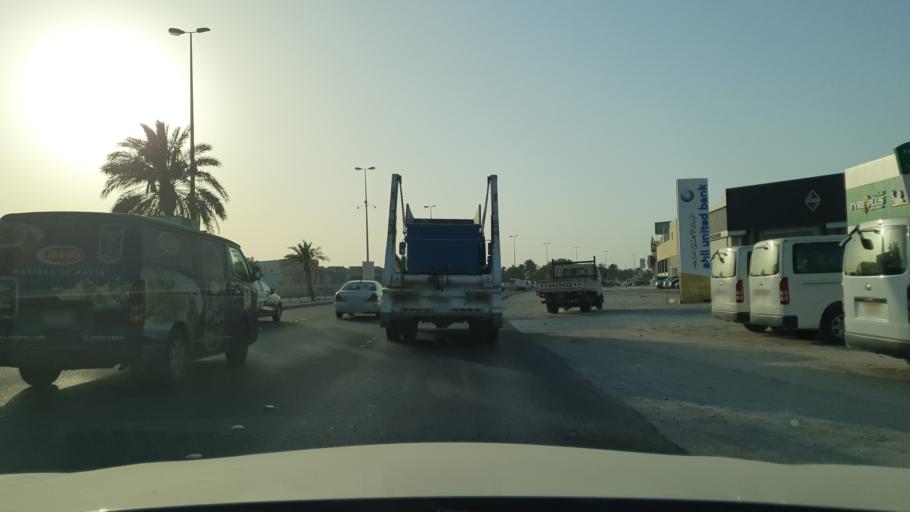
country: BH
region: Northern
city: Sitrah
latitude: 26.1576
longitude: 50.6069
